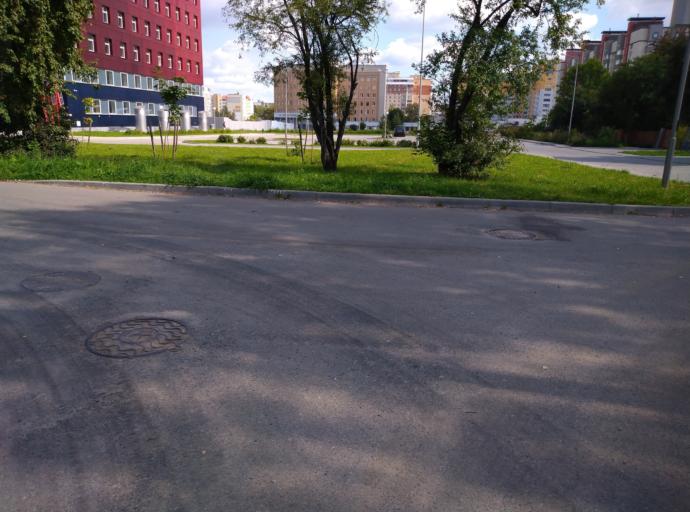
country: BY
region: Minsk
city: Minsk
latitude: 53.8768
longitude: 27.5475
